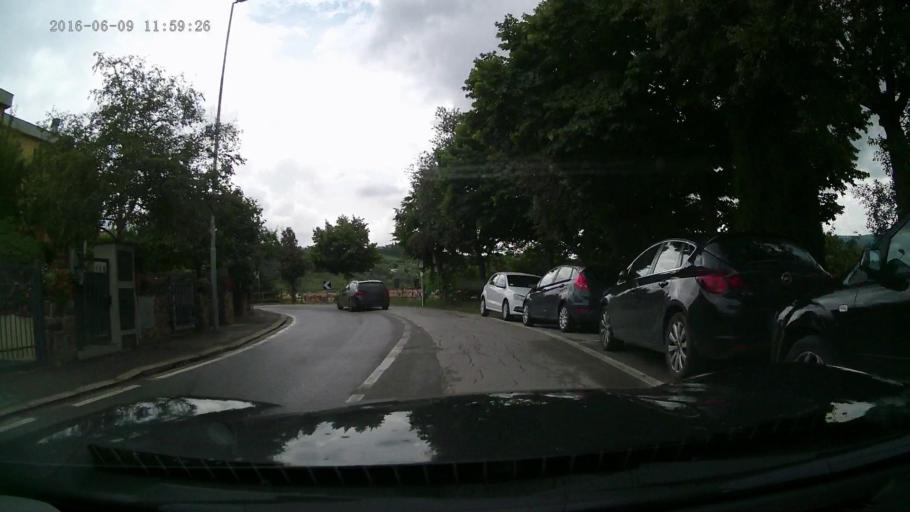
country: IT
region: Tuscany
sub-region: Province of Florence
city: Panzano in Chianti
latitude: 43.5440
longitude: 11.3129
